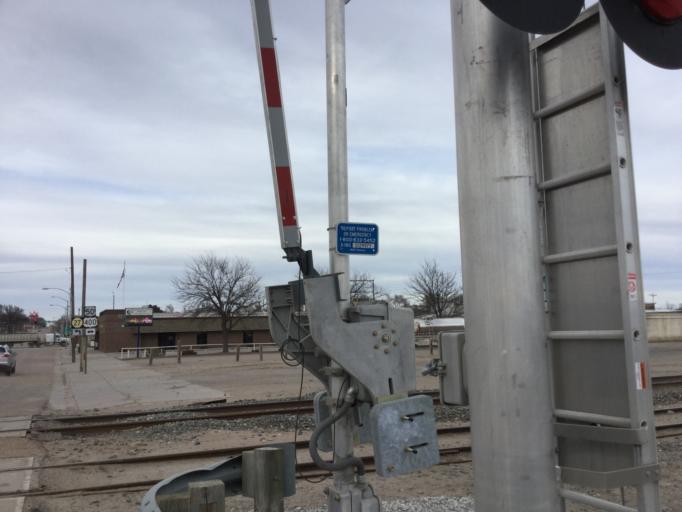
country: US
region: Kansas
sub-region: Hamilton County
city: Syracuse
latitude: 37.9793
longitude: -101.7531
